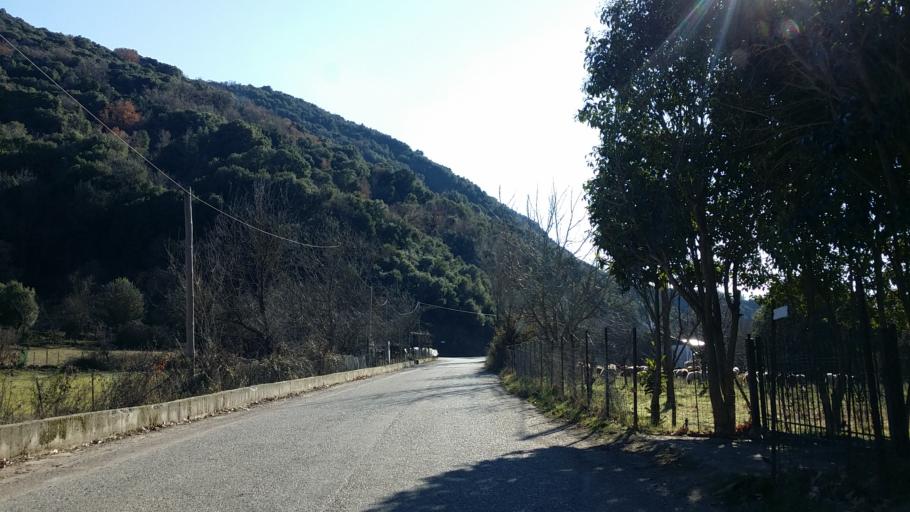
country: GR
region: Central Greece
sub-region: Nomos Evrytanias
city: Kerasochori
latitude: 38.9986
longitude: 21.5729
